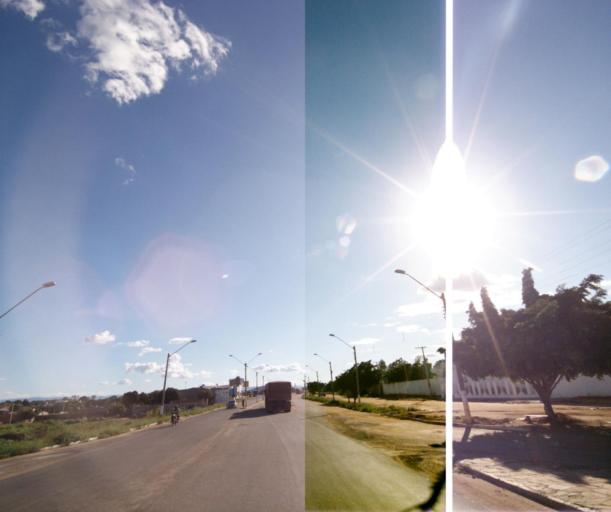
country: BR
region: Bahia
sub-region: Guanambi
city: Guanambi
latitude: -14.2067
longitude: -42.7621
